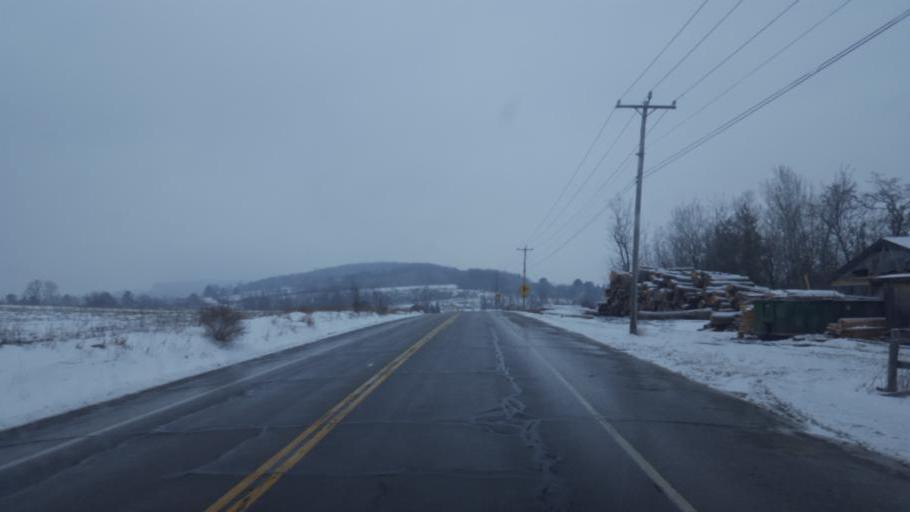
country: US
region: New York
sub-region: Steuben County
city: Canisteo
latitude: 42.1117
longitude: -77.4862
